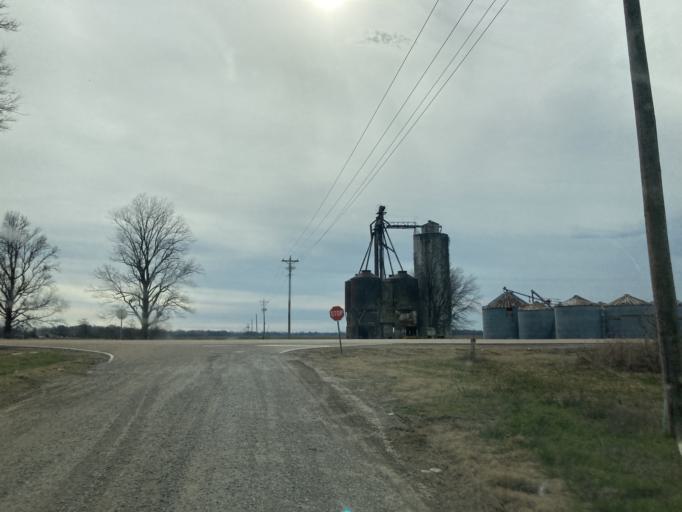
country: US
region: Mississippi
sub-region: Washington County
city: Hollandale
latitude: 33.1841
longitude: -90.6886
